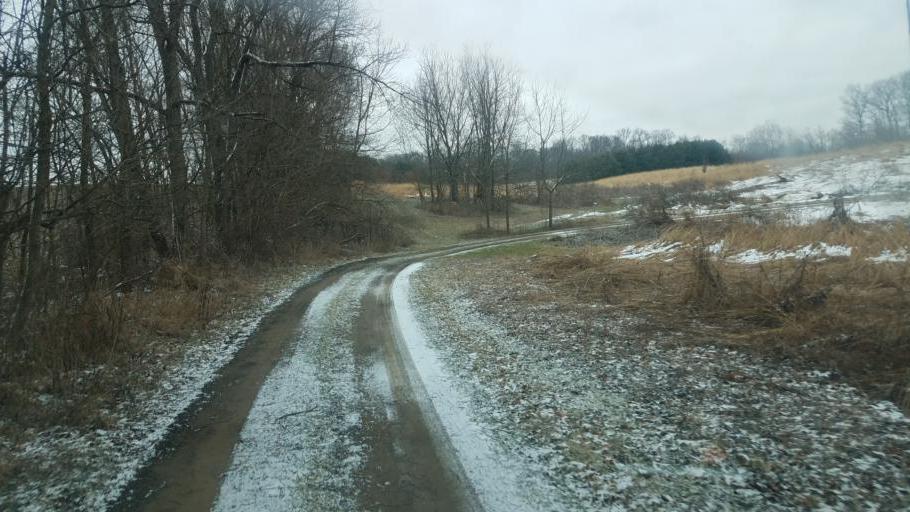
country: US
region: Ohio
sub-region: Knox County
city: Fredericktown
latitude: 40.4671
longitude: -82.6375
